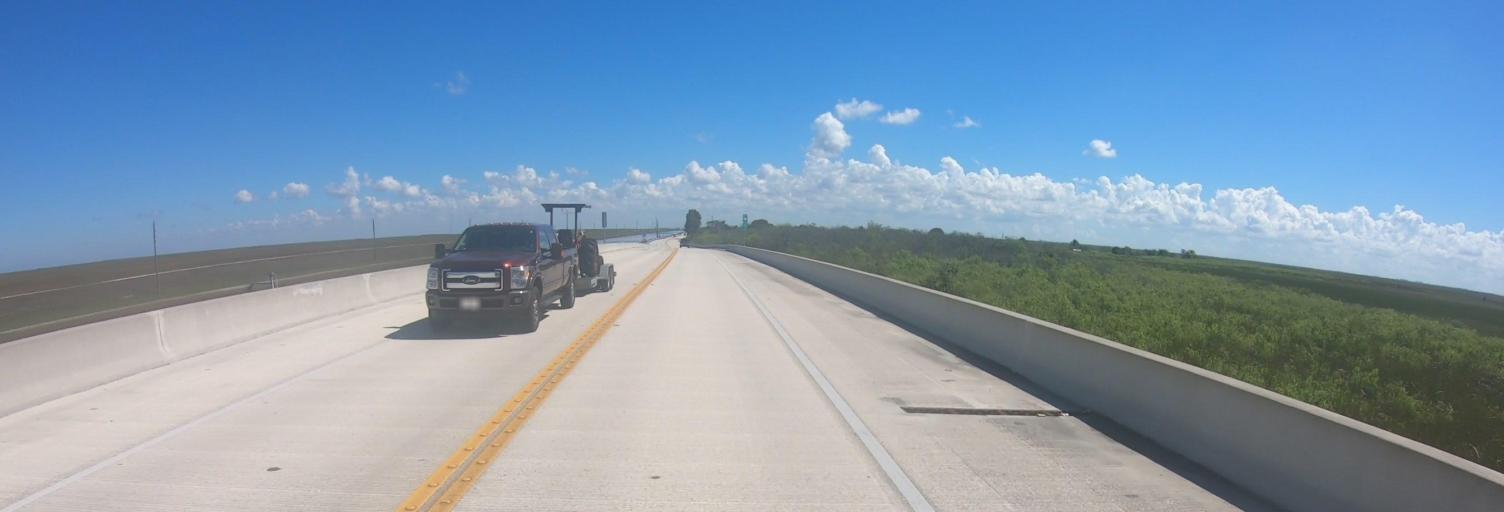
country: US
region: Florida
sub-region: Miami-Dade County
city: Kendall West
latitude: 25.7606
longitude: -80.6093
